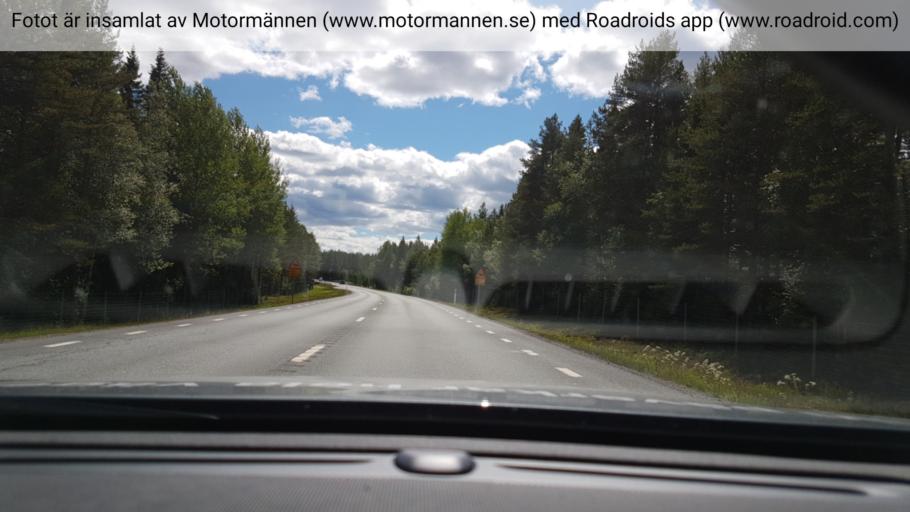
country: SE
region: Vaesterbotten
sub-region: Robertsfors Kommun
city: Robertsfors
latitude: 64.0368
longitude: 20.8432
